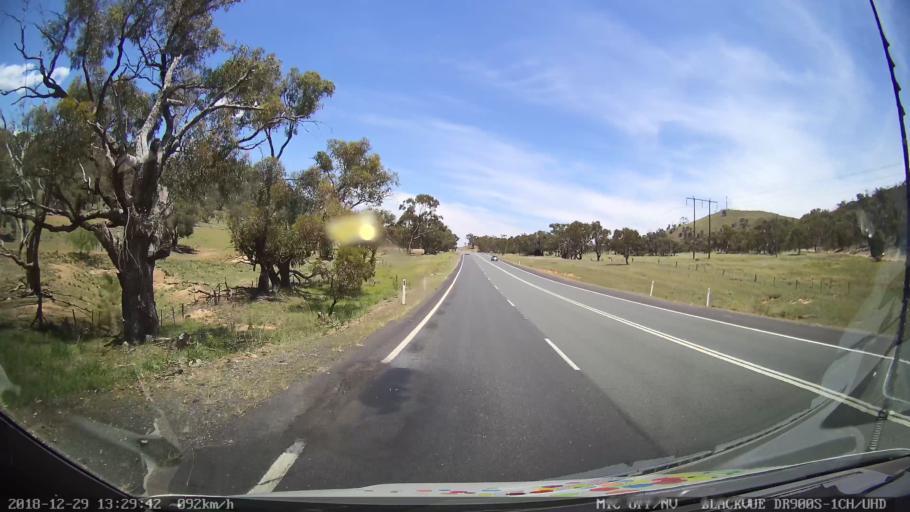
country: AU
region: New South Wales
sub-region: Cooma-Monaro
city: Cooma
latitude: -35.8937
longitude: 149.1612
